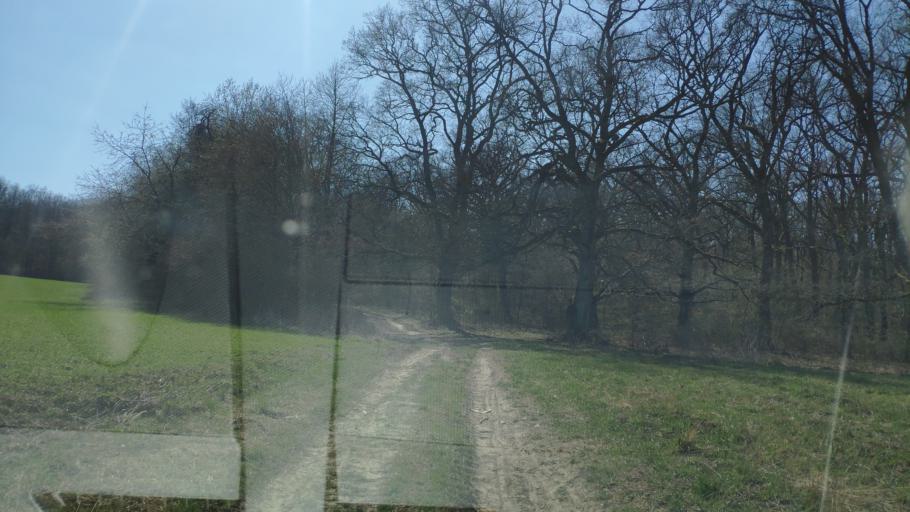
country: SK
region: Kosicky
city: Moldava nad Bodvou
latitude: 48.5677
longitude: 20.9370
